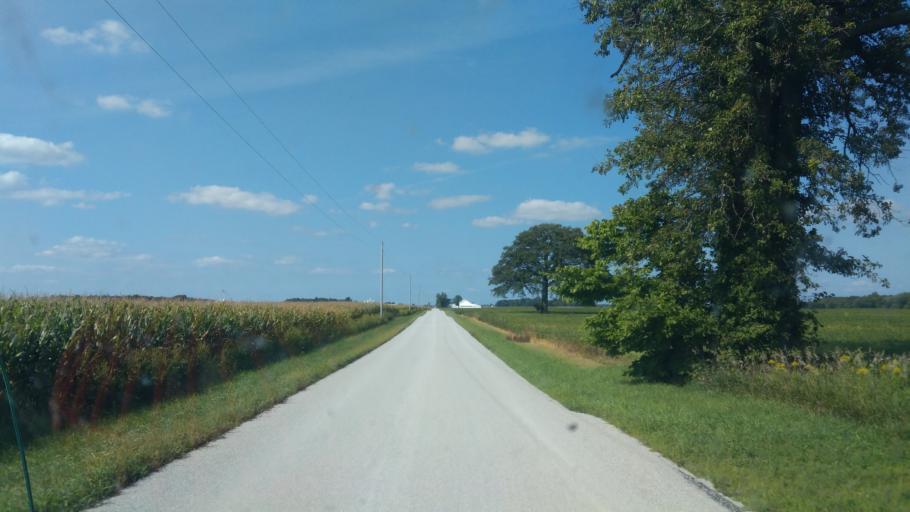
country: US
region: Ohio
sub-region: Hardin County
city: Forest
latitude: 40.6620
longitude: -83.4395
